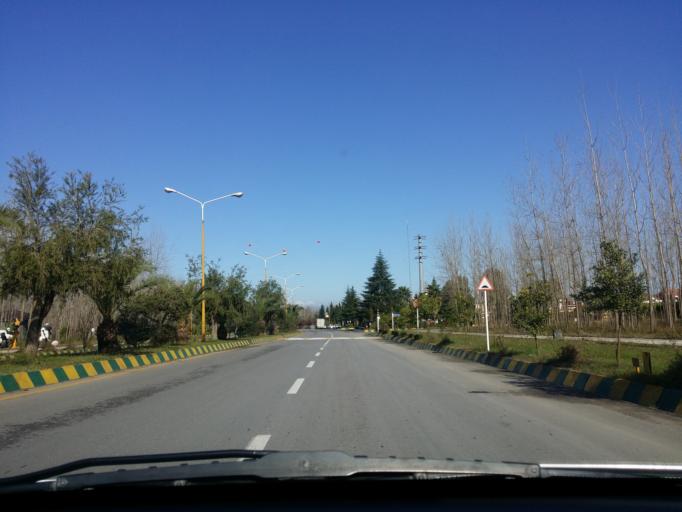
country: IR
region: Mazandaran
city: Chalus
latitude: 36.6744
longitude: 51.3068
